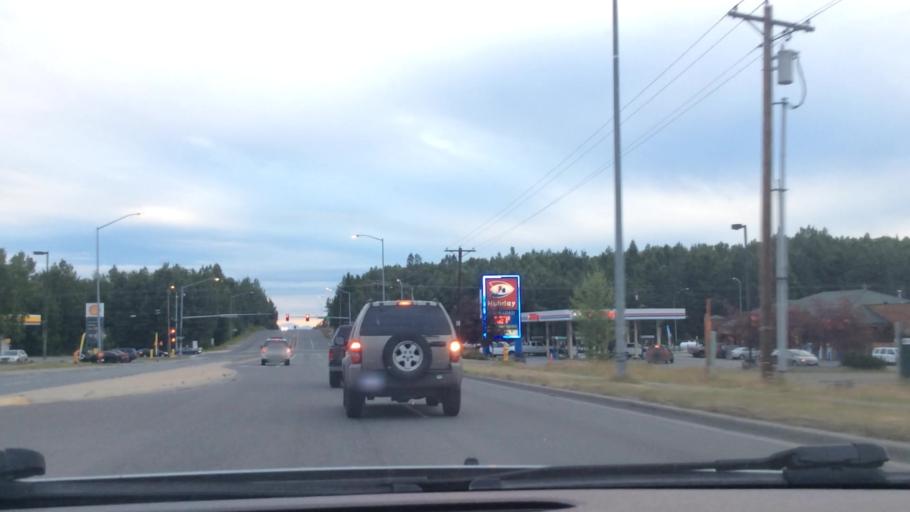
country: US
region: Alaska
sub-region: Anchorage Municipality
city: Anchorage
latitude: 61.2098
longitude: -149.7754
